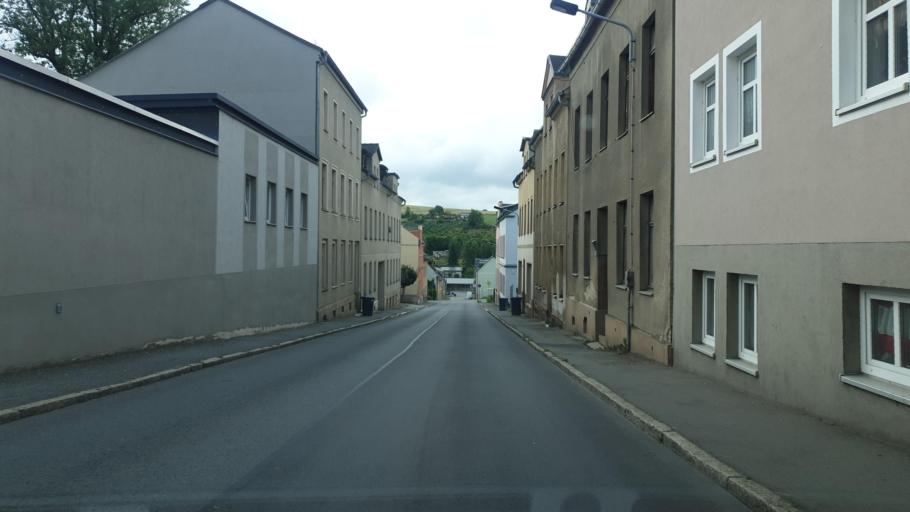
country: DE
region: Saxony
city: Reichenbach/Vogtland
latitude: 50.6232
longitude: 12.3054
